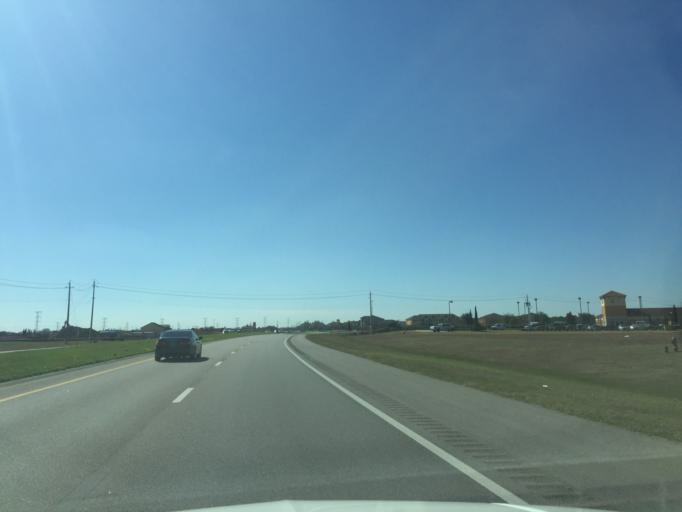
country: US
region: Texas
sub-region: Galveston County
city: Dickinson
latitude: 29.4998
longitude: -95.0495
